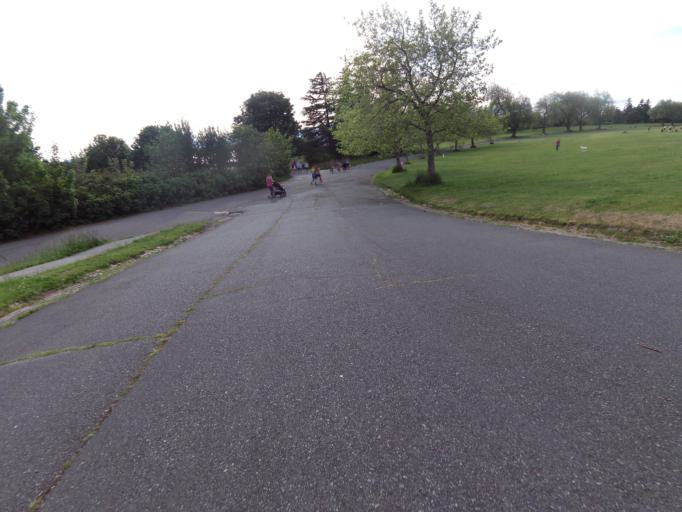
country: US
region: Washington
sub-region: King County
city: Seattle
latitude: 47.6558
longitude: -122.4140
